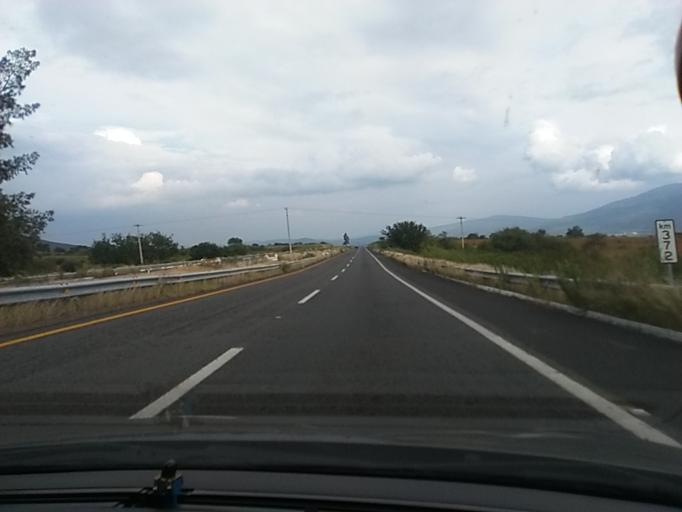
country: MX
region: Michoacan
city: Ixtlan
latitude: 20.1853
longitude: -102.3032
